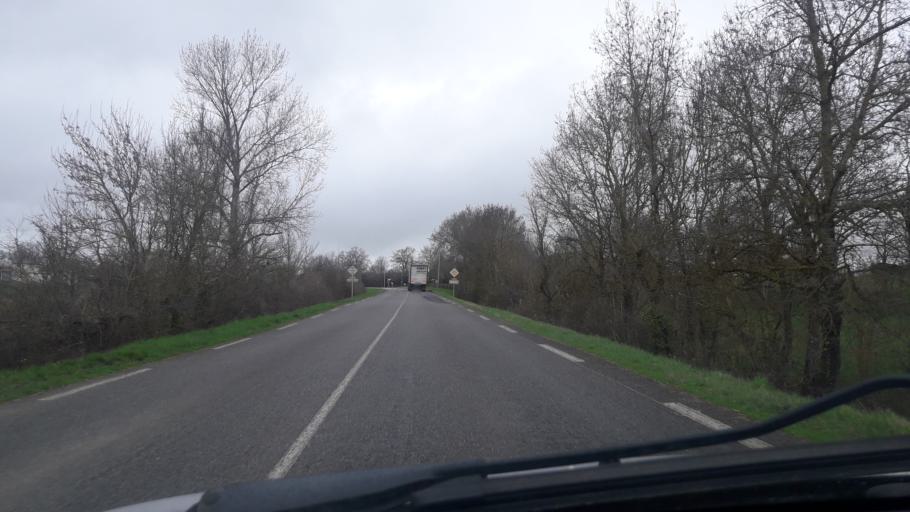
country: FR
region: Midi-Pyrenees
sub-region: Departement du Gers
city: Gimont
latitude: 43.6976
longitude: 0.9978
